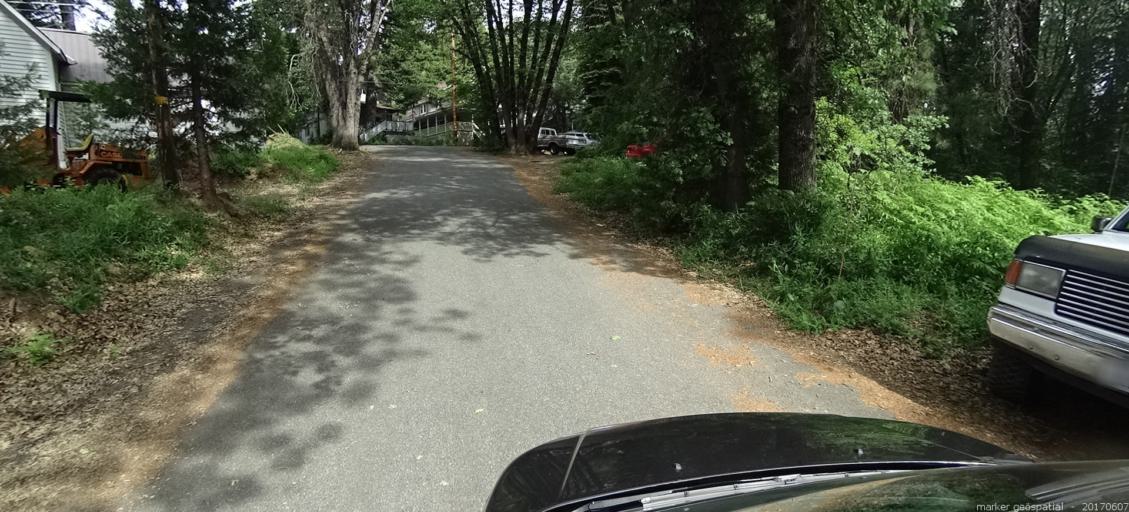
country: US
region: California
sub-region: Siskiyou County
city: McCloud
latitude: 41.2576
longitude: -122.1412
